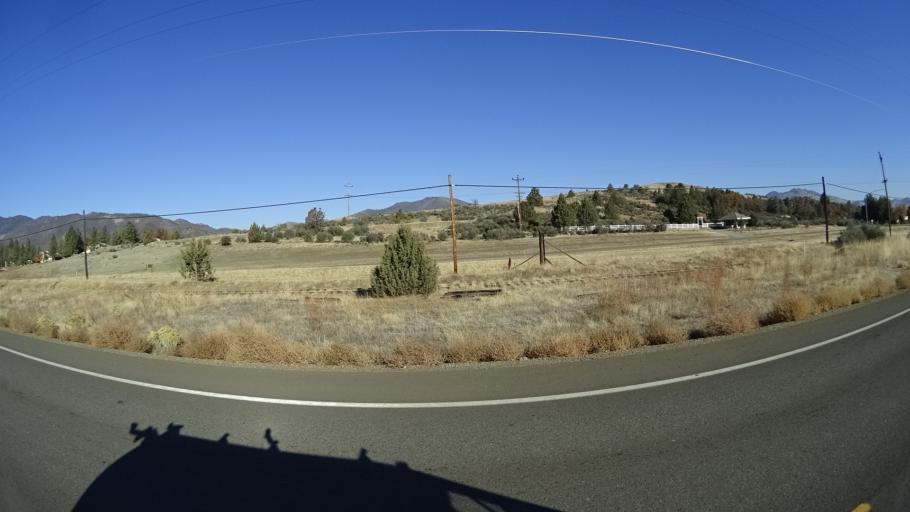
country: US
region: California
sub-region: Siskiyou County
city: Yreka
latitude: 41.7383
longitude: -122.6167
